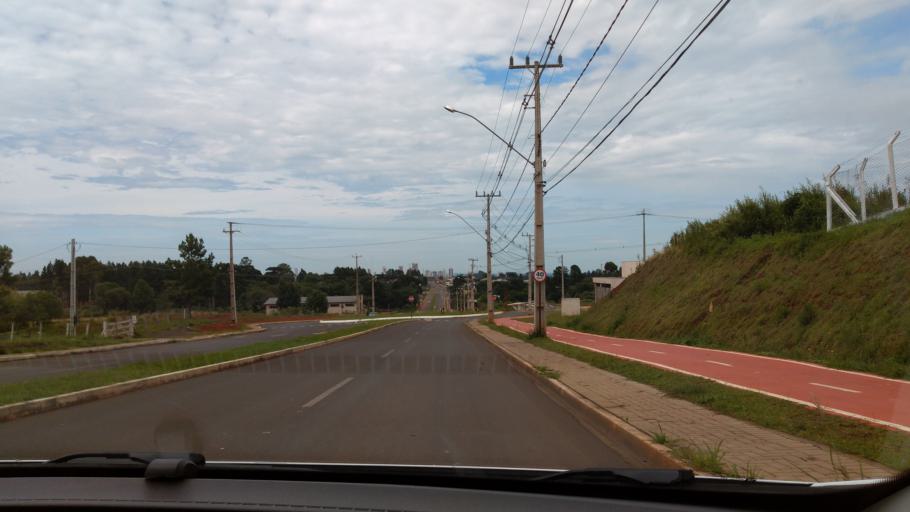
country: BR
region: Parana
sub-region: Guarapuava
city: Guarapuava
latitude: -25.3668
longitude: -51.4357
